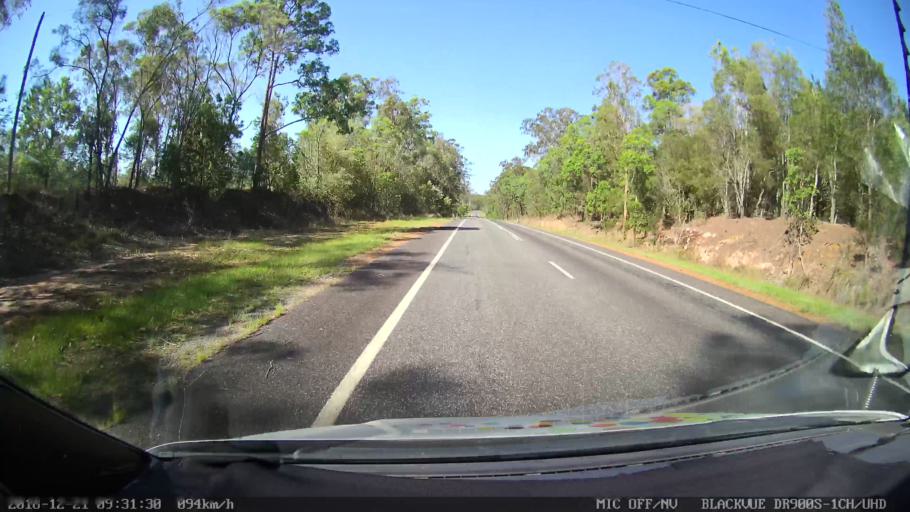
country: AU
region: New South Wales
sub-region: Clarence Valley
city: Maclean
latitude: -29.4606
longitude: 152.9881
